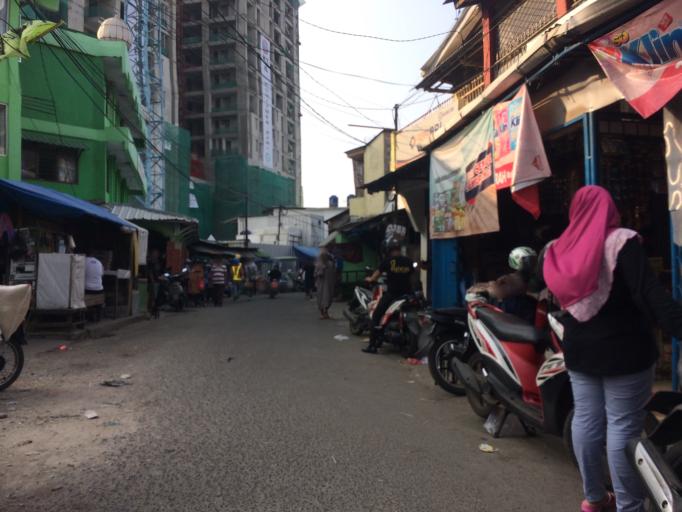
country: ID
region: Jakarta Raya
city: Jakarta
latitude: -6.2085
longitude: 106.8415
